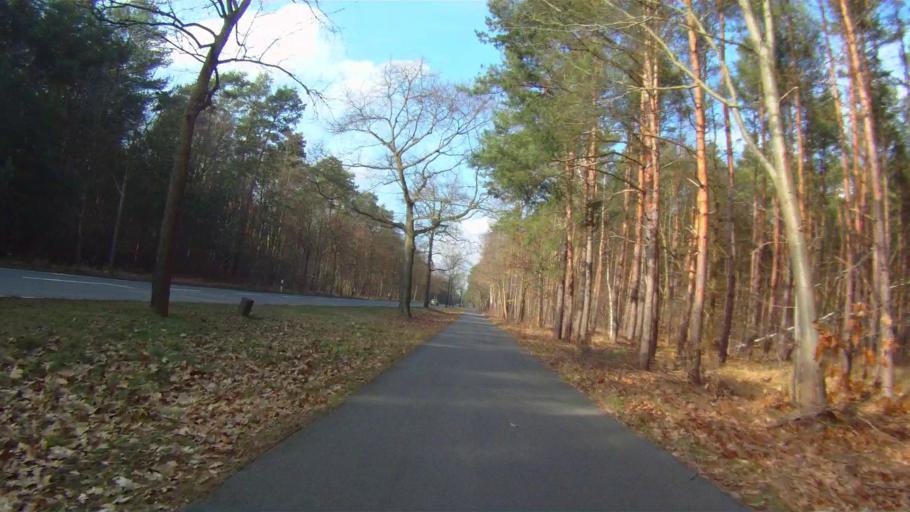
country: DE
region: Brandenburg
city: Zeuthen
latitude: 52.3926
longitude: 13.6192
